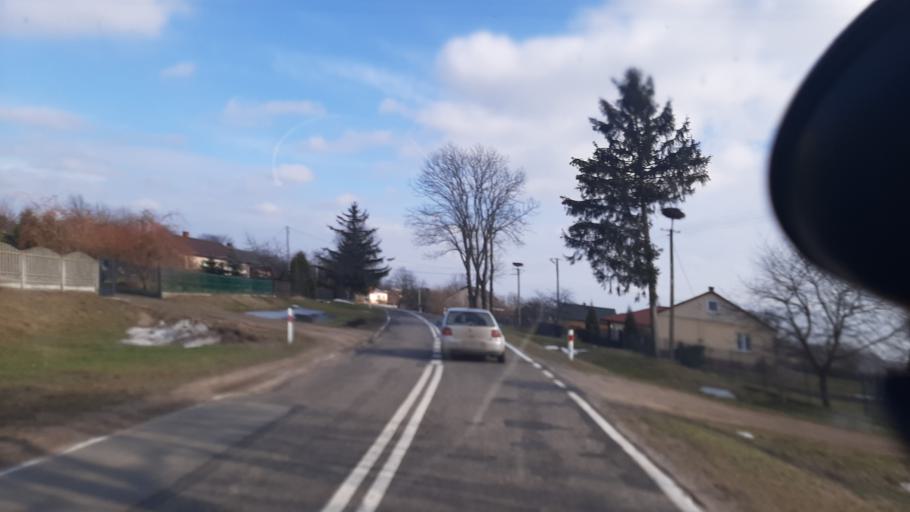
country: PL
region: Lublin Voivodeship
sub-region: Powiat parczewski
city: Sosnowica
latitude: 51.4998
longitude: 23.1520
